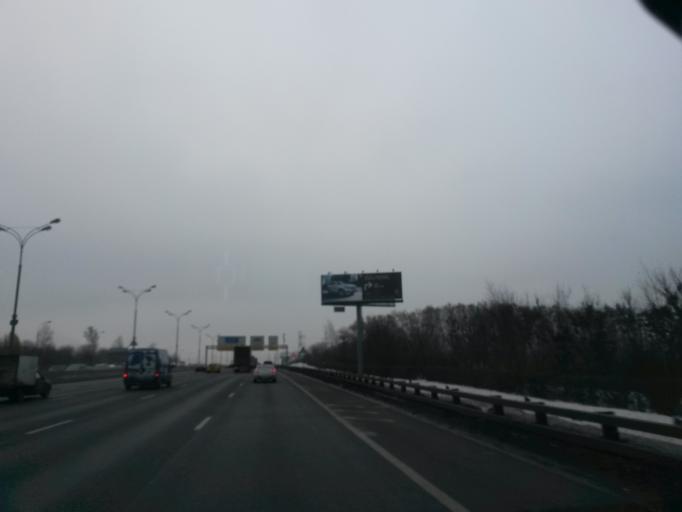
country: RU
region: Moscow
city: Chertanovo Yuzhnoye
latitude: 55.5830
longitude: 37.5637
